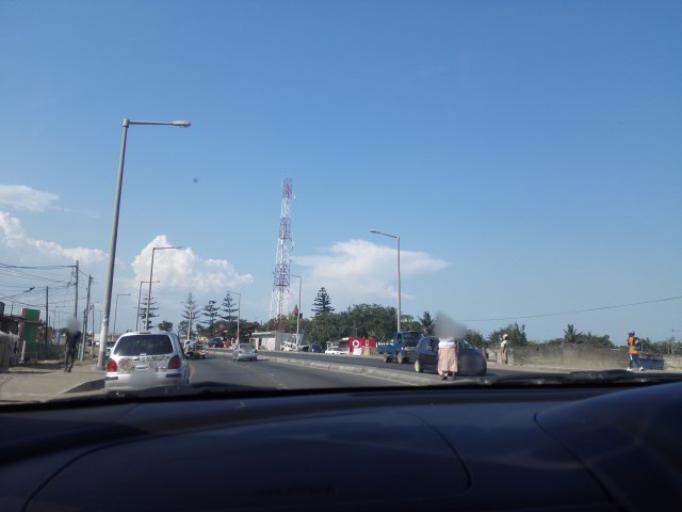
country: MZ
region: Maputo City
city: Maputo
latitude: -25.8819
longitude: 32.5678
